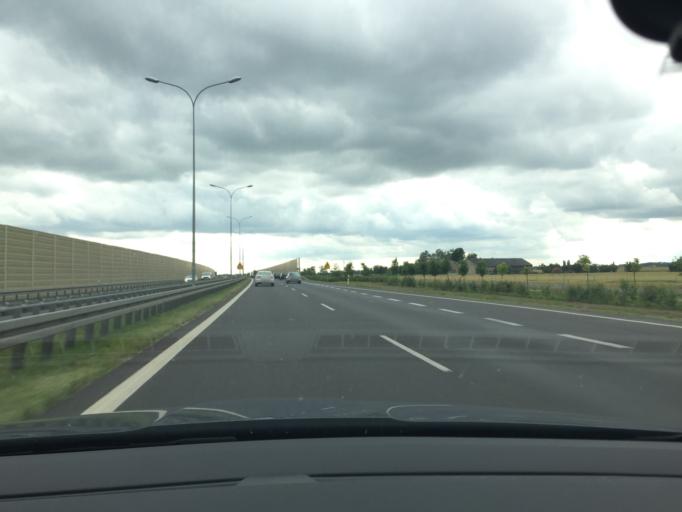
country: PL
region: Greater Poland Voivodeship
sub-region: Powiat poznanski
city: Kleszczewo
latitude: 52.3381
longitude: 17.1589
